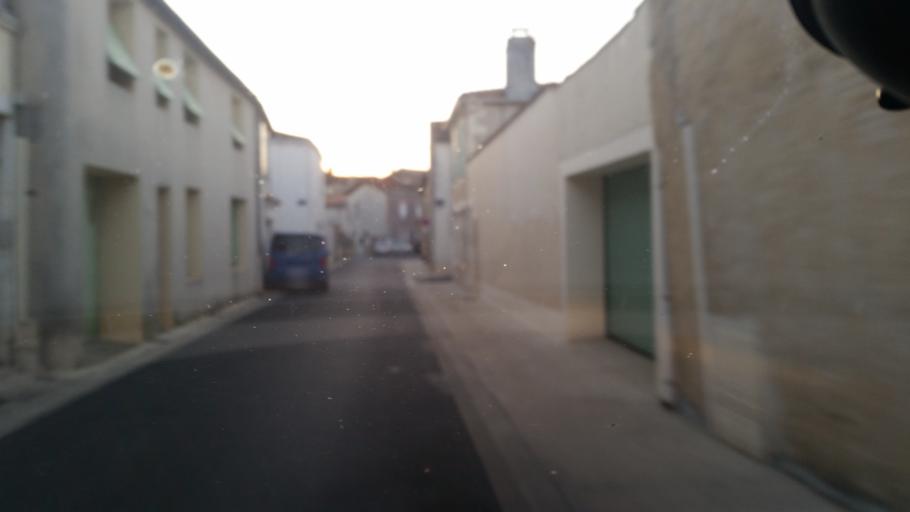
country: FR
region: Poitou-Charentes
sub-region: Departement de la Charente-Maritime
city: Marans
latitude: 46.3104
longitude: -0.9947
